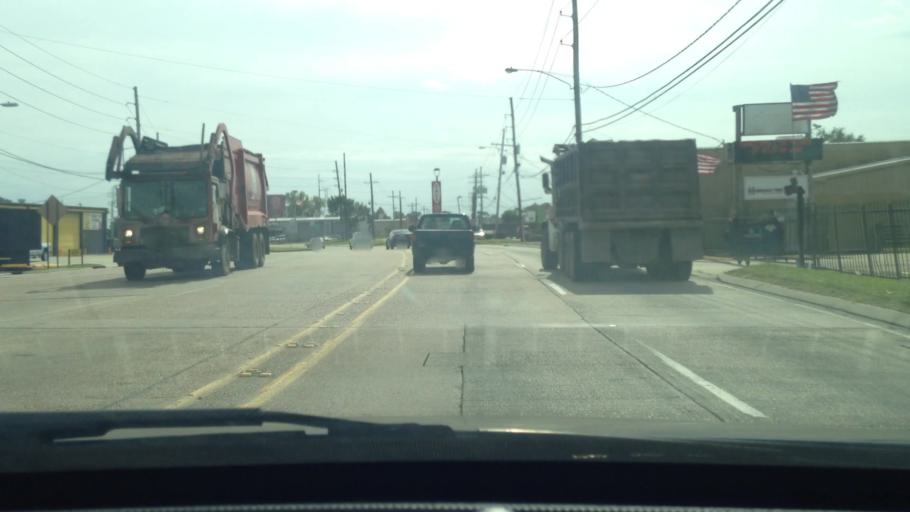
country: US
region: Louisiana
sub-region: Jefferson Parish
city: River Ridge
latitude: 29.9770
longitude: -90.2106
